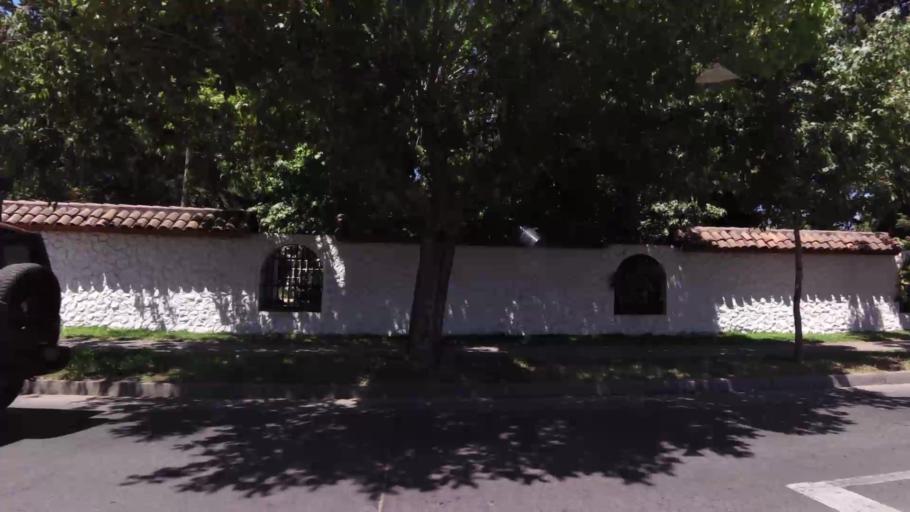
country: CL
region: Maule
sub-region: Provincia de Curico
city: Curico
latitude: -34.9847
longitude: -71.2232
